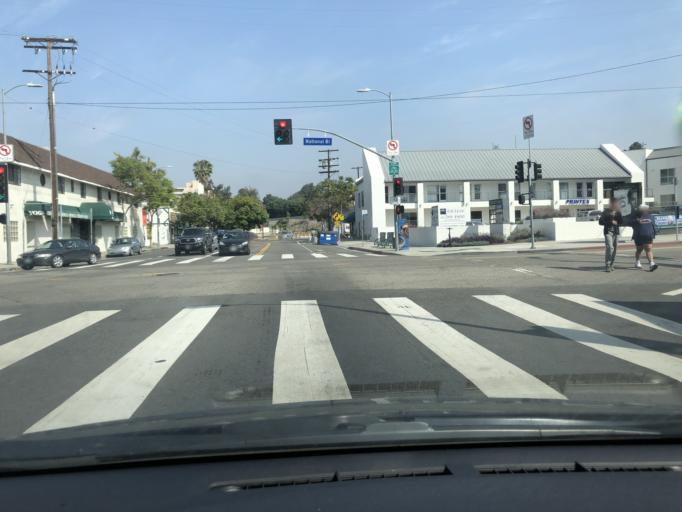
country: US
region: California
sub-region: Los Angeles County
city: Culver City
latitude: 34.0292
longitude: -118.4106
